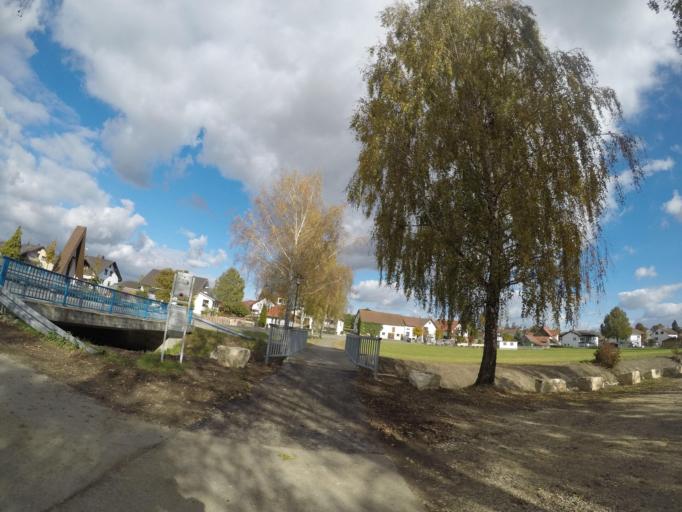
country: DE
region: Baden-Wuerttemberg
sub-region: Tuebingen Region
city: Oberstadion
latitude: 48.1895
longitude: 9.6991
